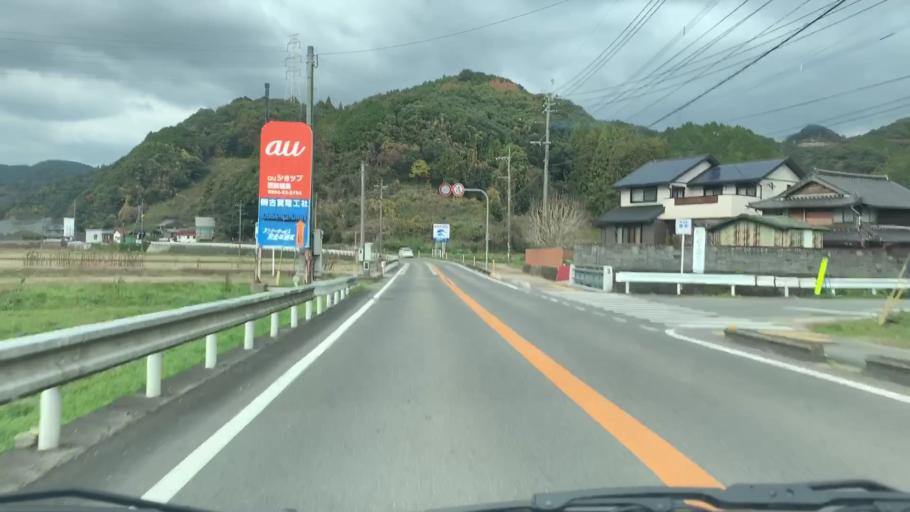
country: JP
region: Saga Prefecture
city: Ureshinomachi-shimojuku
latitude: 33.1337
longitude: 130.0300
